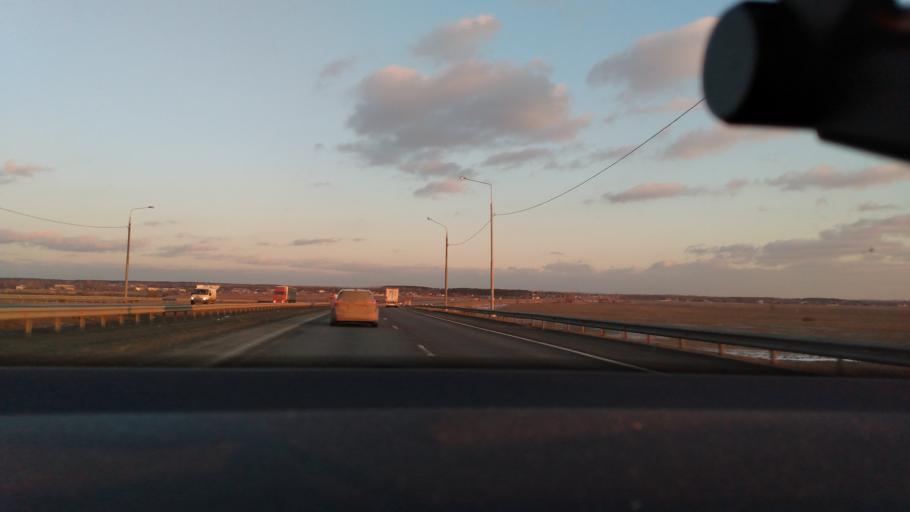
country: RU
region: Moskovskaya
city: Raduzhnyy
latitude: 55.1410
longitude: 38.7505
